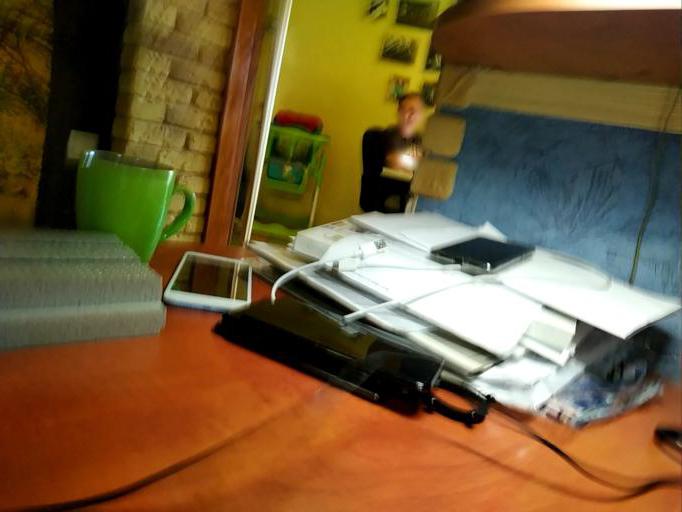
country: RU
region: Tverskaya
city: Sandovo
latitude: 58.4583
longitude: 36.4209
